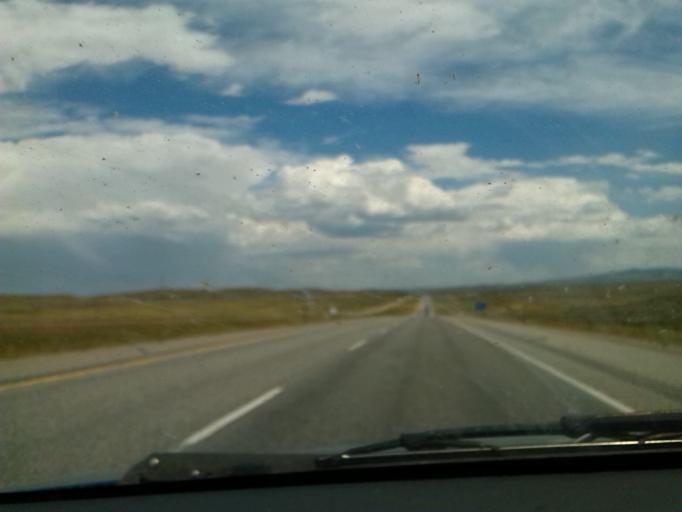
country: US
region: Wyoming
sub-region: Carbon County
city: Saratoga
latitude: 41.7324
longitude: -106.4823
